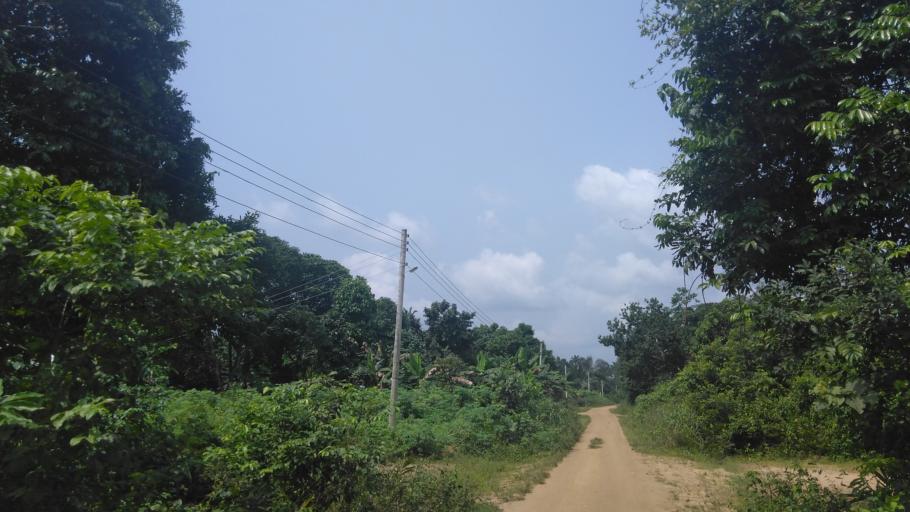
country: NG
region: Abia
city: Aba
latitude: 5.0433
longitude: 7.2358
